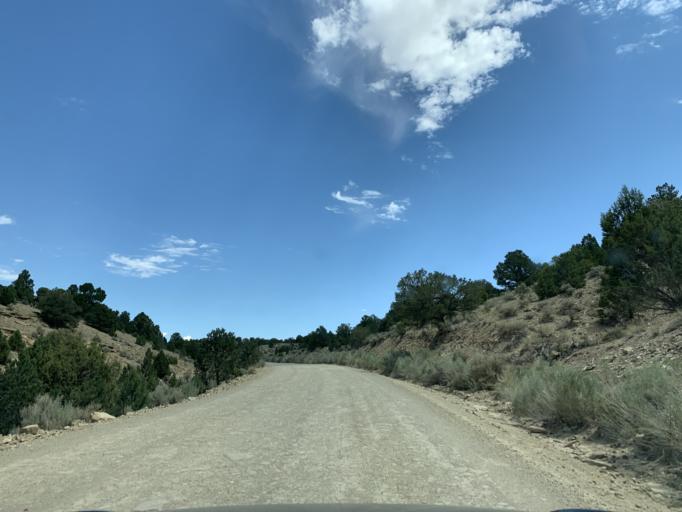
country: US
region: Utah
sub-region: Duchesne County
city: Duchesne
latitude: 39.8774
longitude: -110.2349
